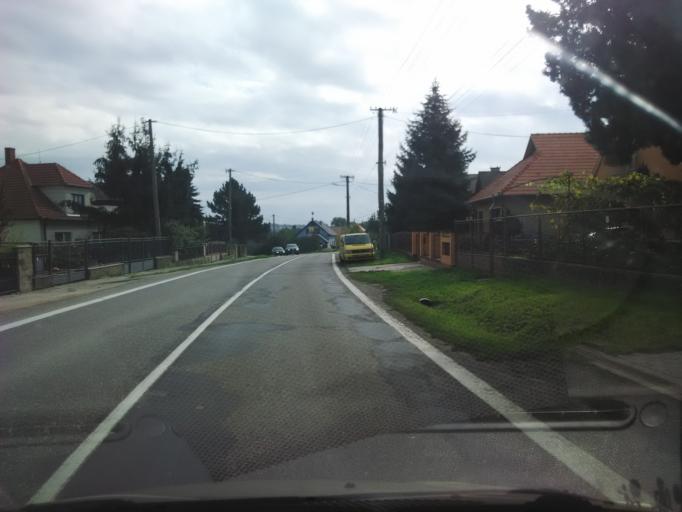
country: SK
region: Nitriansky
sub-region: Okres Nitra
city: Nitra
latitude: 48.2929
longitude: 18.1801
